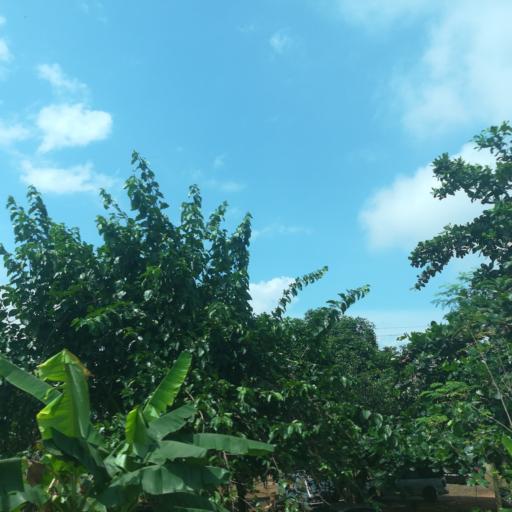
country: NG
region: Lagos
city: Ikorodu
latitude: 6.6624
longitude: 3.6783
